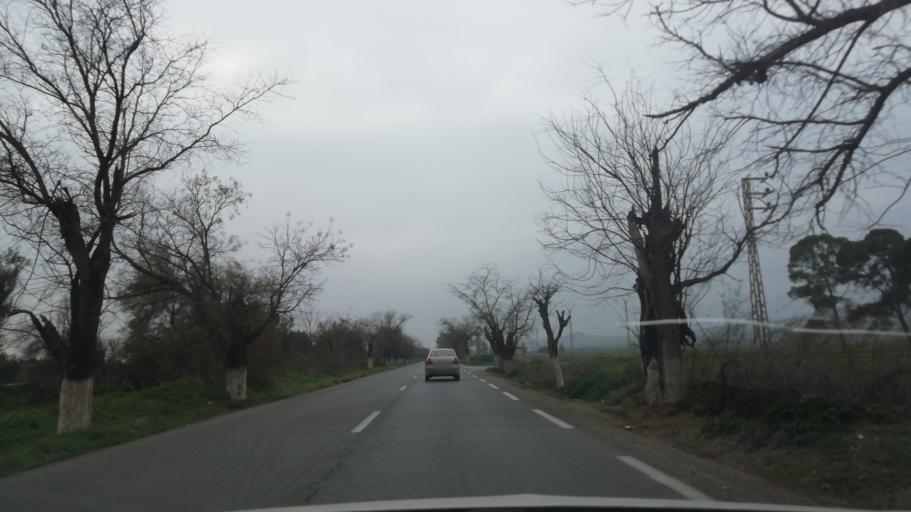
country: DZ
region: Sidi Bel Abbes
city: Sfizef
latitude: 35.2227
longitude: -0.2856
